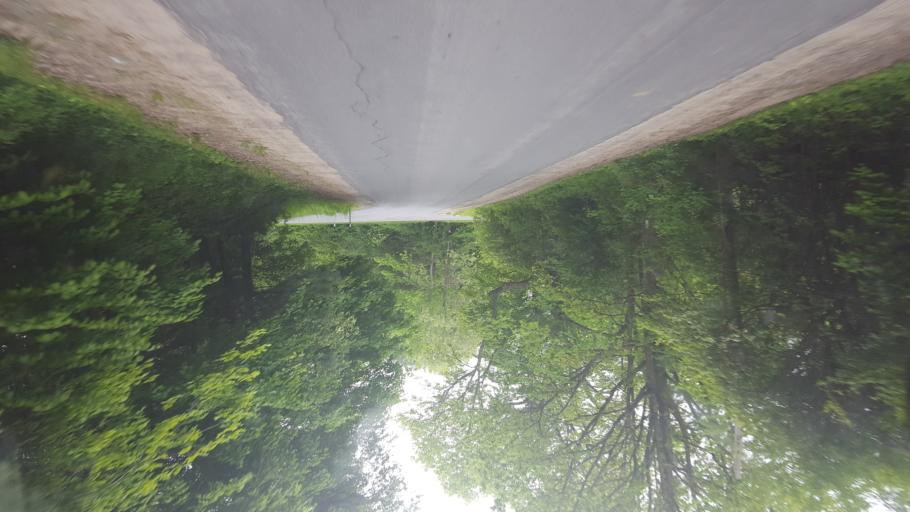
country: US
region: New York
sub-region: Otsego County
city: Richfield Springs
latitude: 42.8789
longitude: -75.1661
